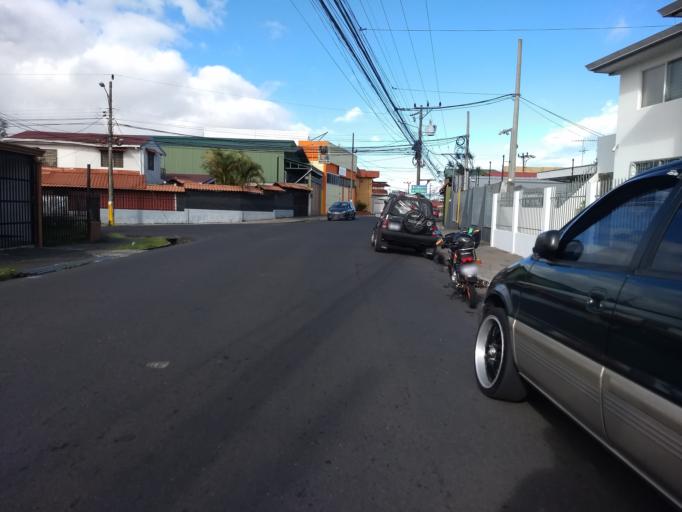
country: CR
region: San Jose
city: Calle Blancos
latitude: 9.9638
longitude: -84.0675
